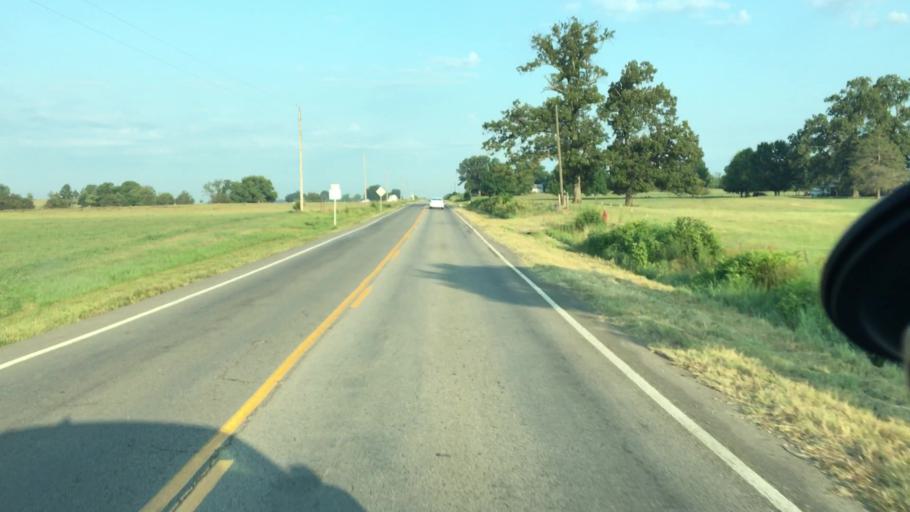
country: US
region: Arkansas
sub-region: Johnson County
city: Clarksville
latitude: 35.3786
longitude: -93.5315
